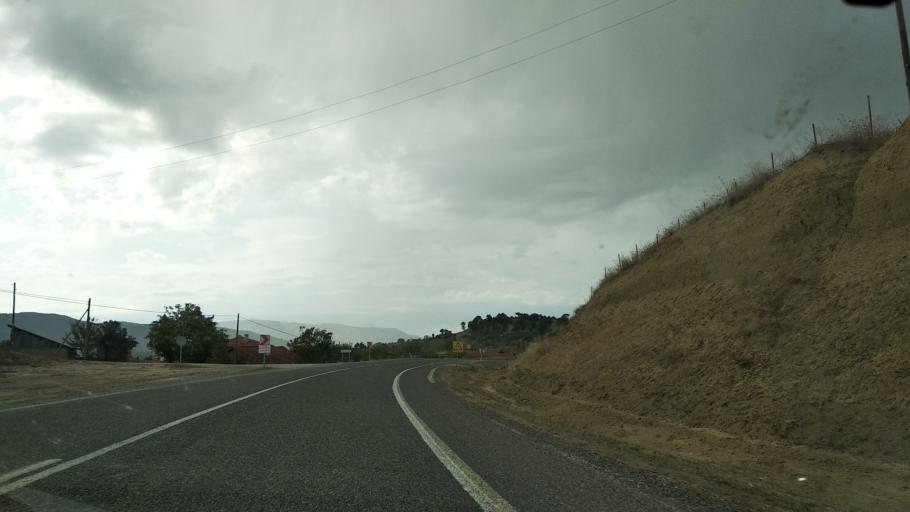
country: TR
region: Bolu
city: Seben
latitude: 40.3345
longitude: 31.4683
